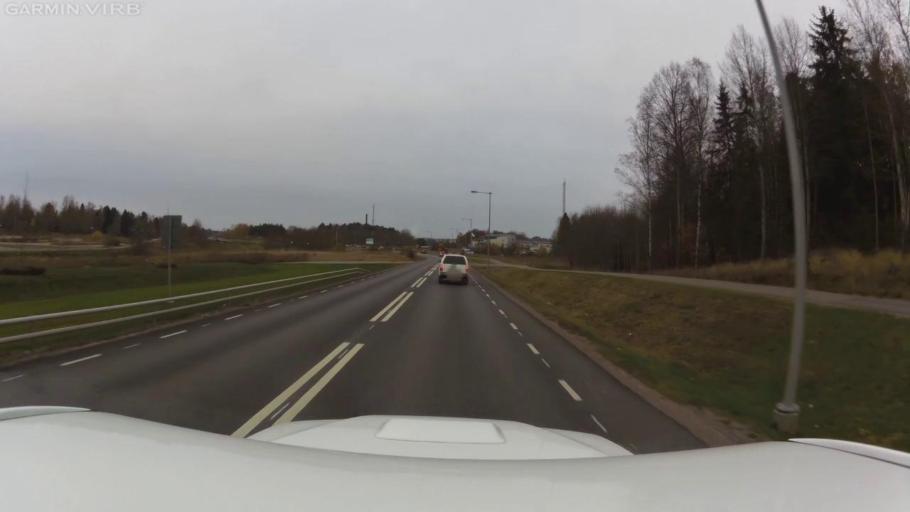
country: SE
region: OEstergoetland
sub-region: Linkopings Kommun
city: Linkoping
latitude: 58.3886
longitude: 15.5865
